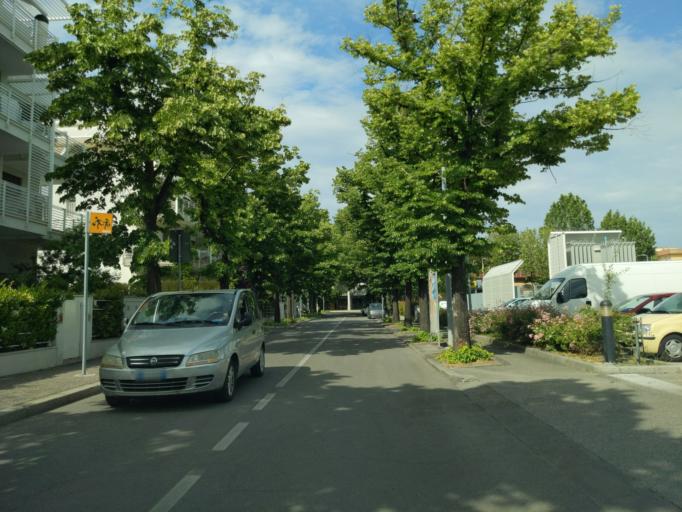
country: IT
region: Emilia-Romagna
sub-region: Provincia di Rimini
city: Rimini
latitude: 44.0462
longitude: 12.5812
